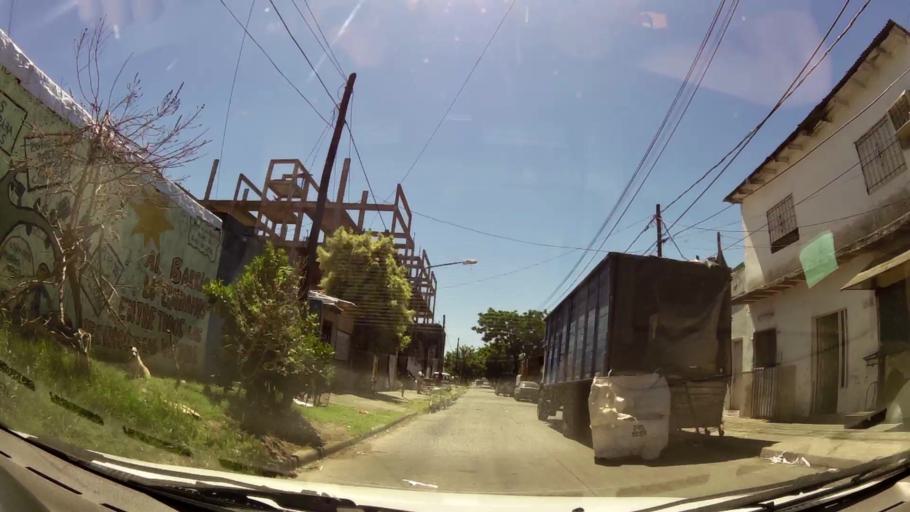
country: AR
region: Buenos Aires
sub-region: Partido de Vicente Lopez
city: Olivos
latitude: -34.5151
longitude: -58.5125
